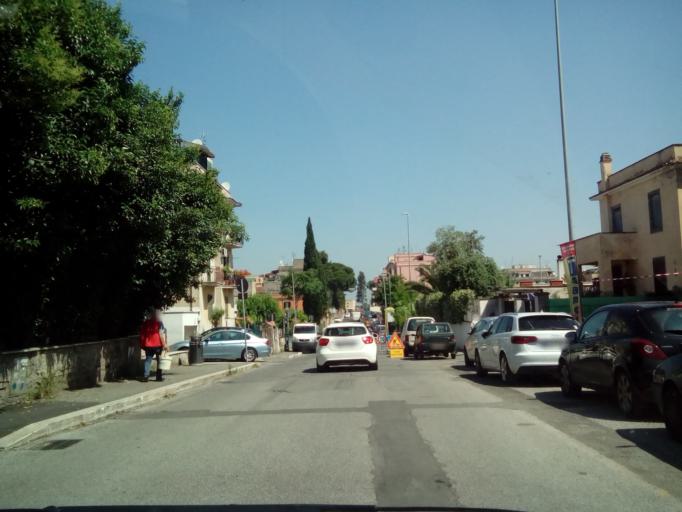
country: IT
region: Latium
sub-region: Citta metropolitana di Roma Capitale
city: Rome
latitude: 41.8842
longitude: 12.5770
